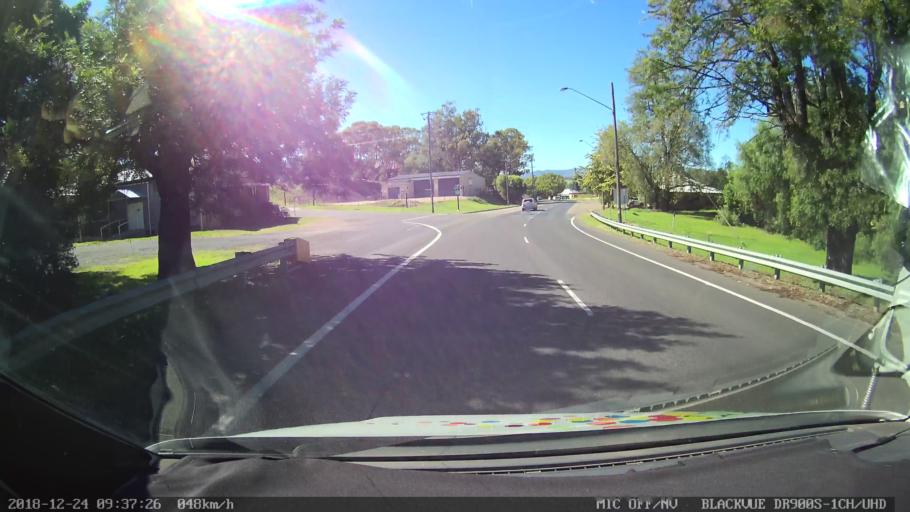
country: AU
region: New South Wales
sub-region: Liverpool Plains
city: Quirindi
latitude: -31.6449
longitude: 150.7257
